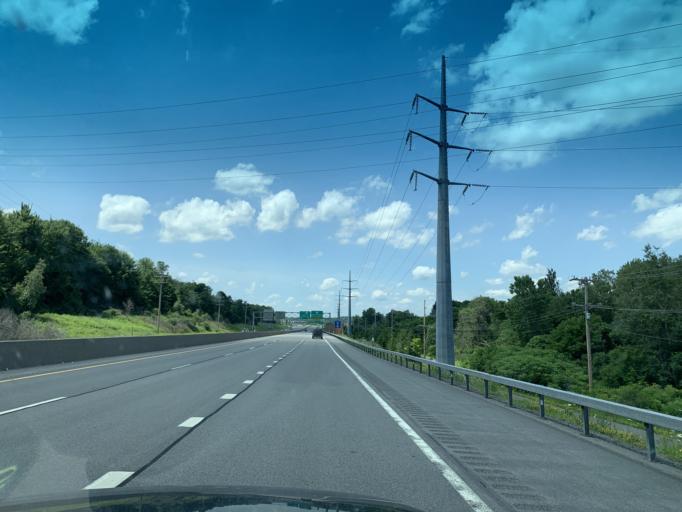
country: US
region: New York
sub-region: Oneida County
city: New Hartford
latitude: 43.0852
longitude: -75.2979
